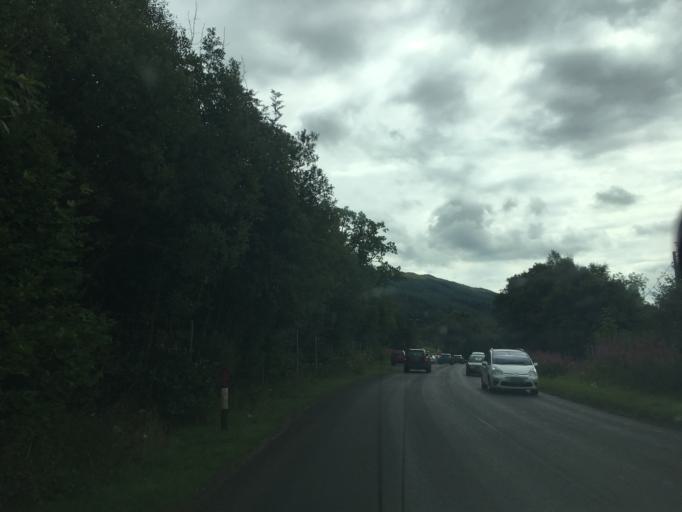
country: GB
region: Scotland
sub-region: Stirling
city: Callander
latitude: 56.2954
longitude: -4.2923
